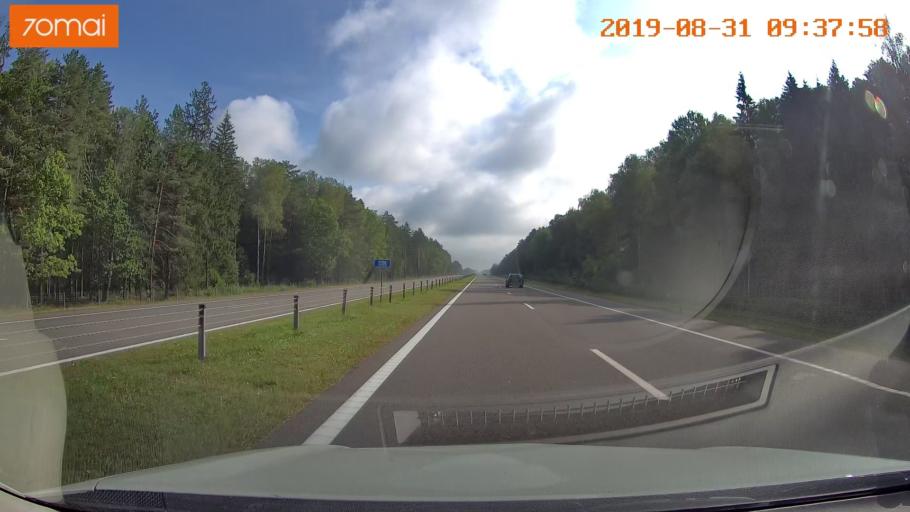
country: BY
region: Minsk
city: Byerazino
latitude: 53.8978
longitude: 29.3494
